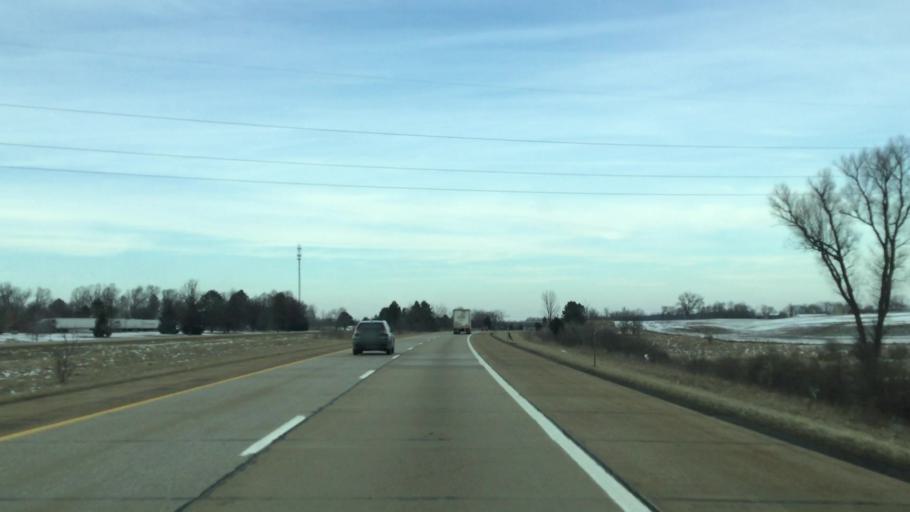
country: US
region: Michigan
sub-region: Calhoun County
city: Marshall
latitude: 42.3263
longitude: -84.9910
